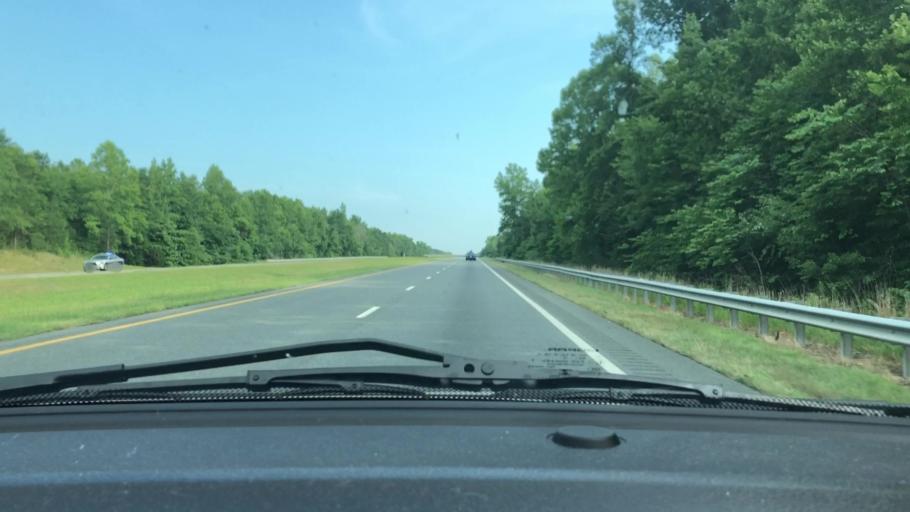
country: US
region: North Carolina
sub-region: Guilford County
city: Forest Oaks
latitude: 35.9417
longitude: -79.6872
